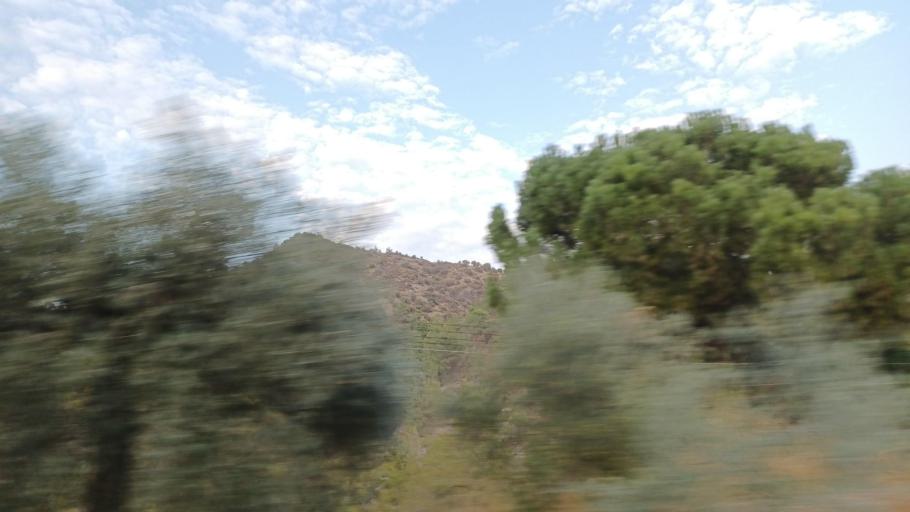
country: CY
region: Limassol
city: Pelendri
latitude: 34.8526
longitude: 32.9504
